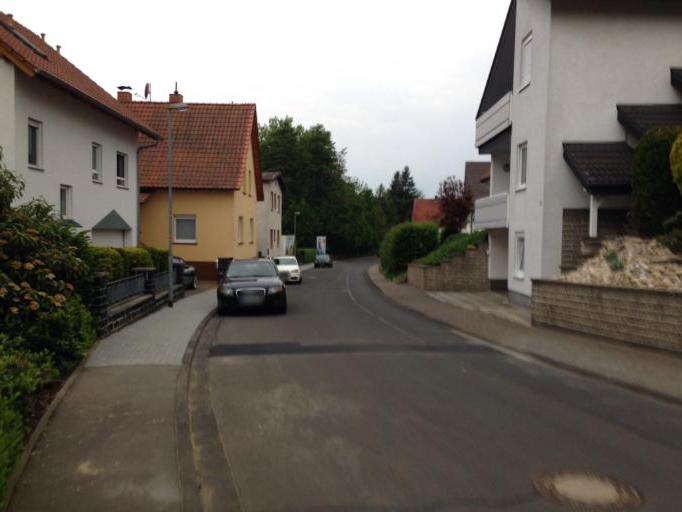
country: DE
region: Hesse
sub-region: Regierungsbezirk Giessen
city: Alten Buseck
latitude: 50.6093
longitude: 8.7569
